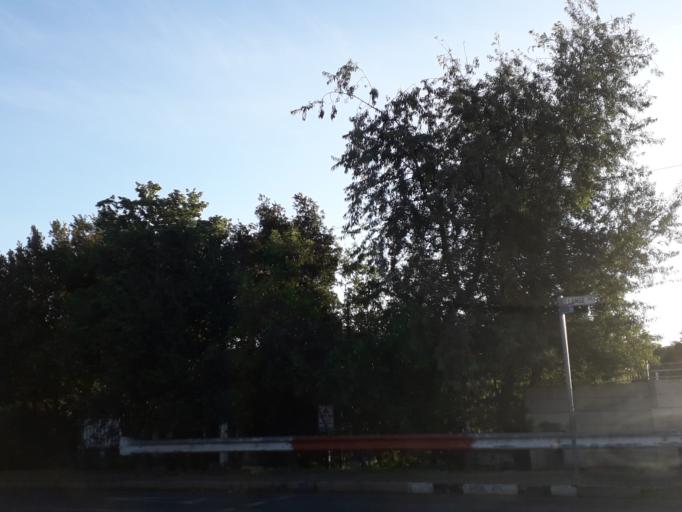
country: ZA
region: Gauteng
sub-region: City of Johannesburg Metropolitan Municipality
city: Roodepoort
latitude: -26.1618
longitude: 27.9416
